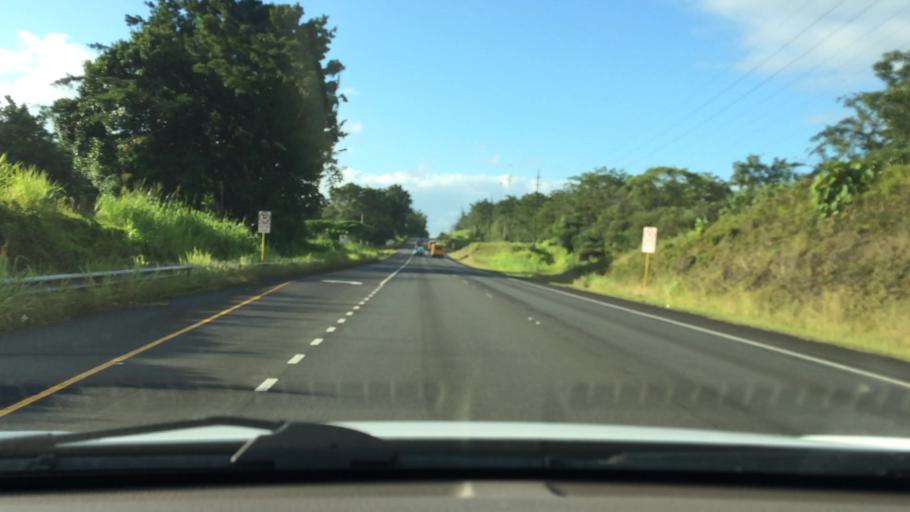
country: US
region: Hawaii
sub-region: Hawaii County
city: Kea'au
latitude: 19.6469
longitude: -155.0494
